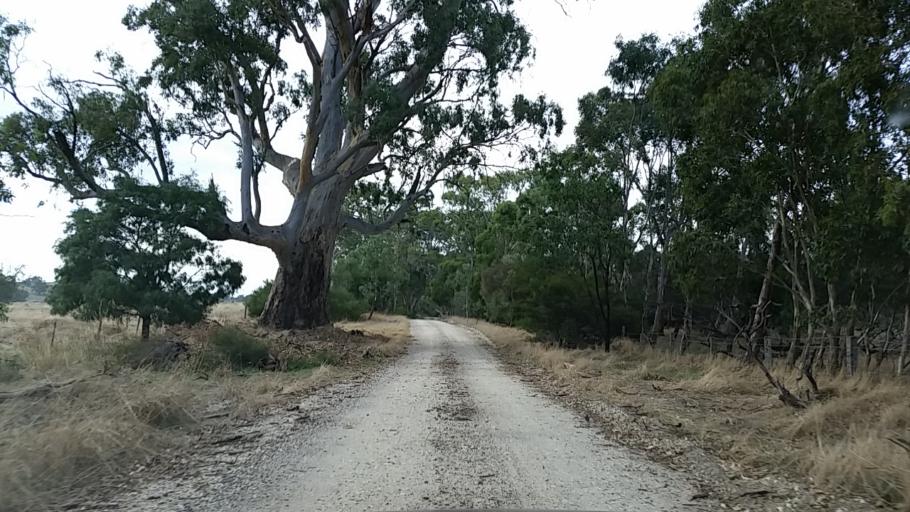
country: AU
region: South Australia
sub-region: Barossa
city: Angaston
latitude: -34.5680
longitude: 139.0744
